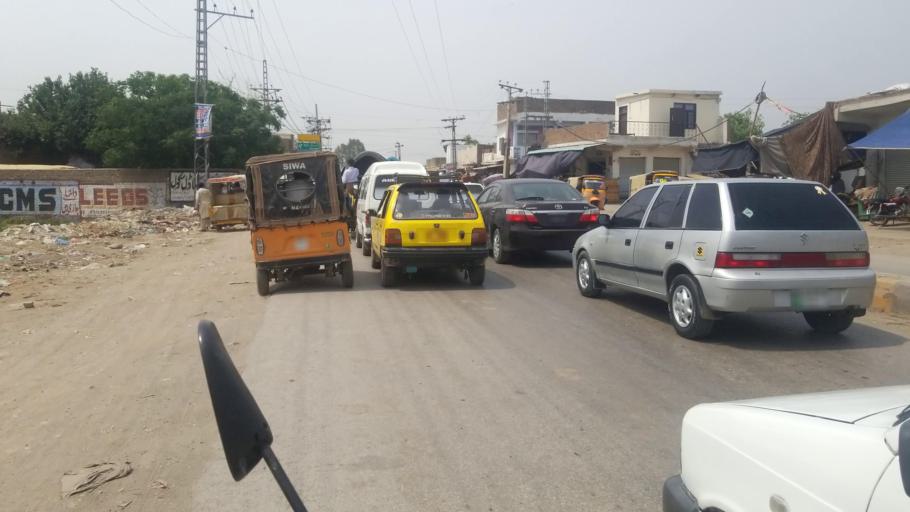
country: PK
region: Khyber Pakhtunkhwa
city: Peshawar
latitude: 33.9961
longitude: 71.6080
